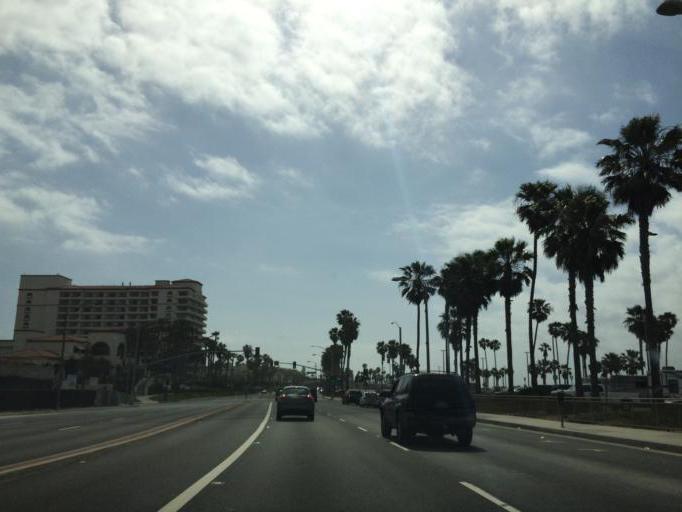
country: US
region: California
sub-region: Orange County
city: Huntington Beach
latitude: 33.6536
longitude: -117.9965
